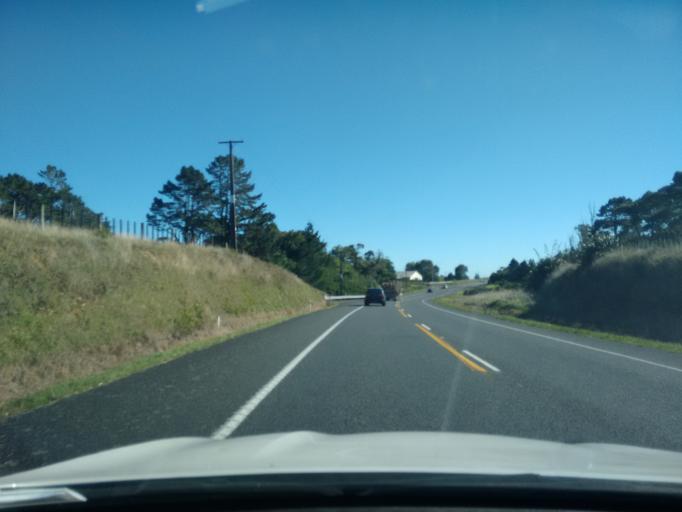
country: NZ
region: Taranaki
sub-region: New Plymouth District
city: New Plymouth
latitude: -39.1318
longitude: 174.1215
